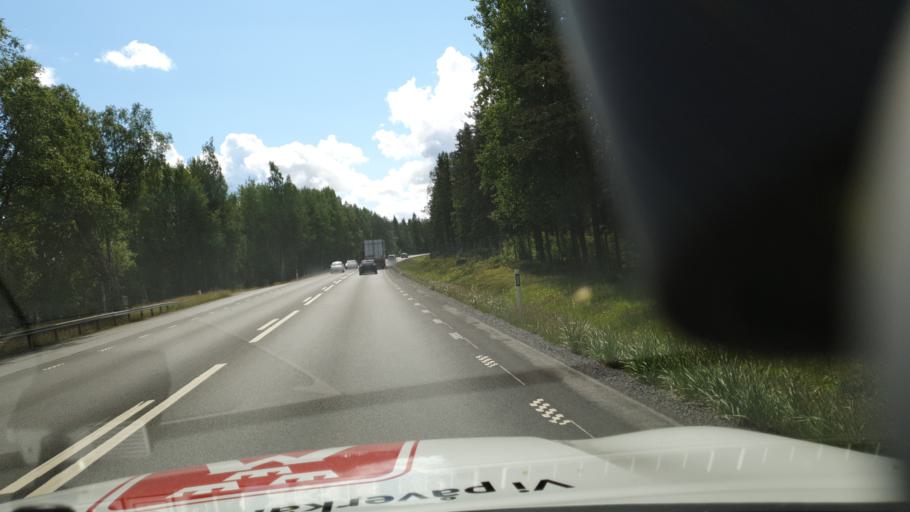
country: SE
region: Vaesterbotten
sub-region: Skelleftea Kommun
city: Burea
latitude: 64.5384
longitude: 21.2568
